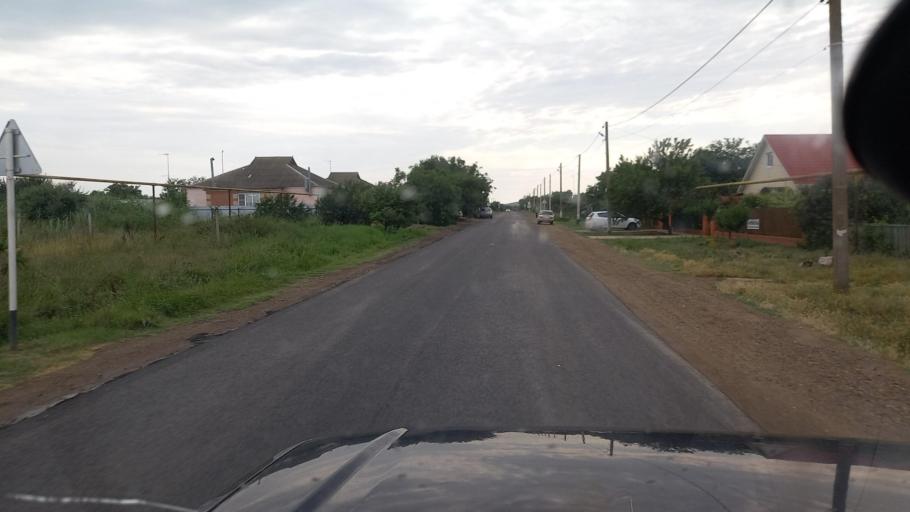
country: RU
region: Krasnodarskiy
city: Akhtanizovskaya
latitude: 45.3331
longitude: 37.1195
